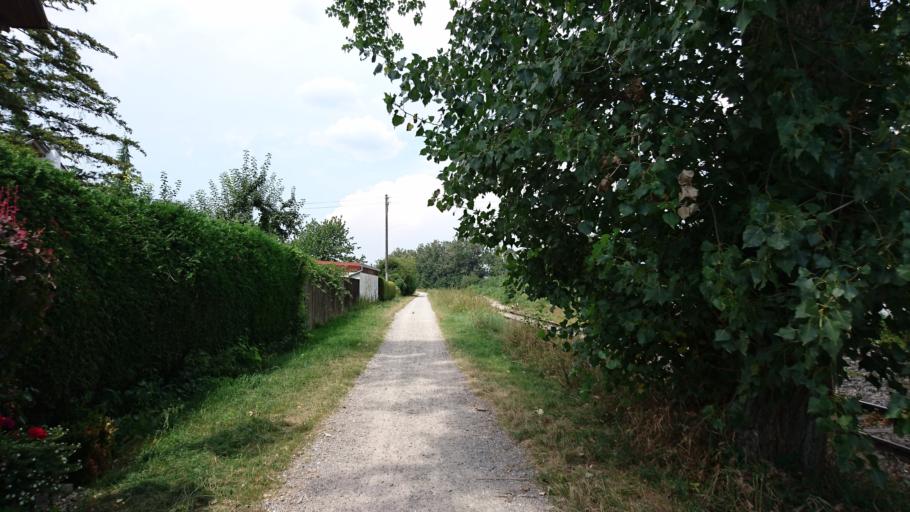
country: DE
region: Bavaria
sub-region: Swabia
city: Augsburg
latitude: 48.3893
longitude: 10.9285
